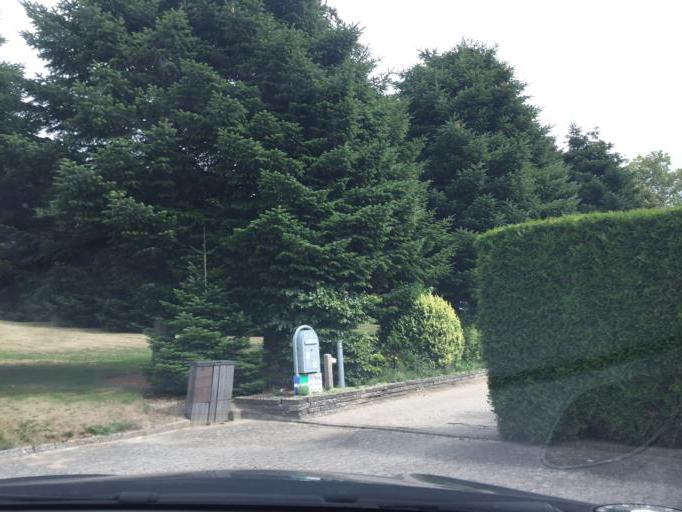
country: DK
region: South Denmark
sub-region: Assens Kommune
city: Arup
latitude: 55.3785
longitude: 10.0441
